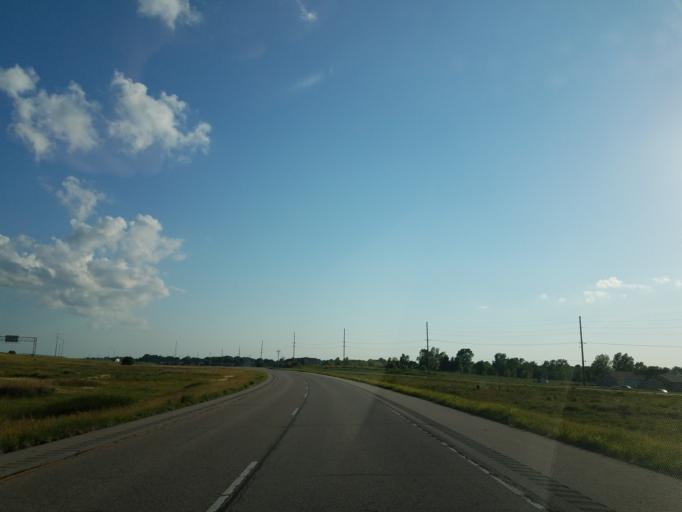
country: US
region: Illinois
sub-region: McLean County
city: Bloomington
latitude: 40.4387
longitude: -89.0252
